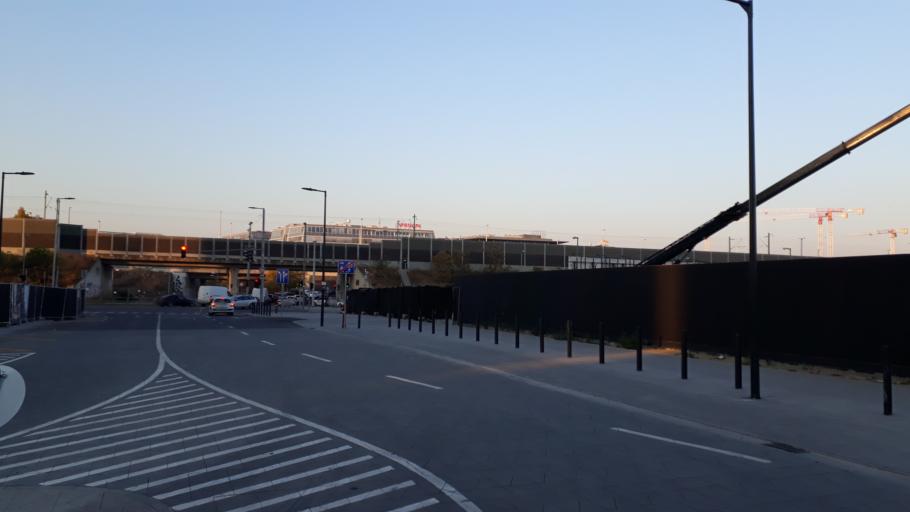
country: HU
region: Budapest
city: Budapest IX. keruelet
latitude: 47.4675
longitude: 19.0589
